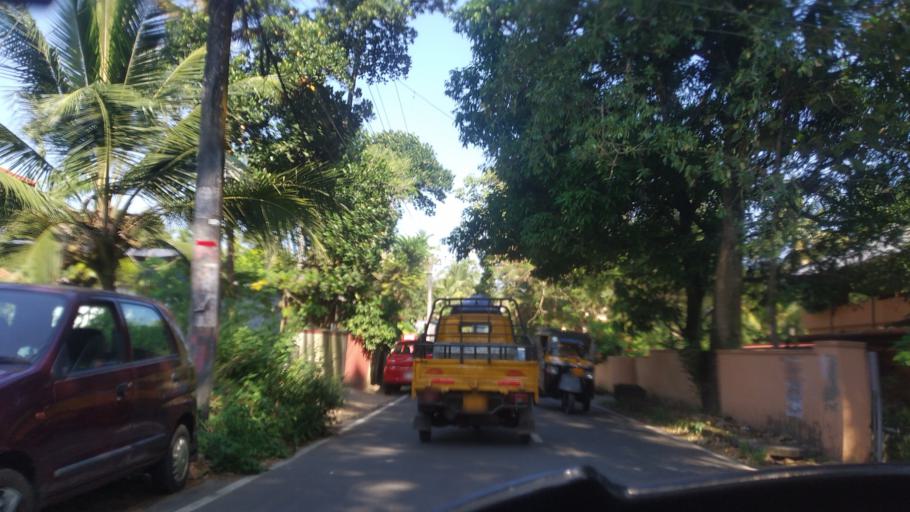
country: IN
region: Kerala
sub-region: Ernakulam
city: Elur
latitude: 10.1144
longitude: 76.2479
